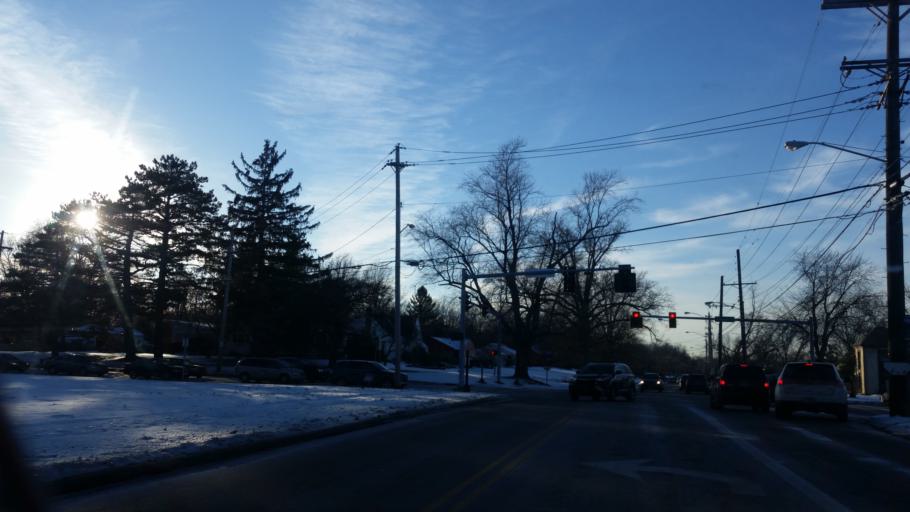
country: US
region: Ohio
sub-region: Cuyahoga County
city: Fairview Park
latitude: 41.4715
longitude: -81.8818
